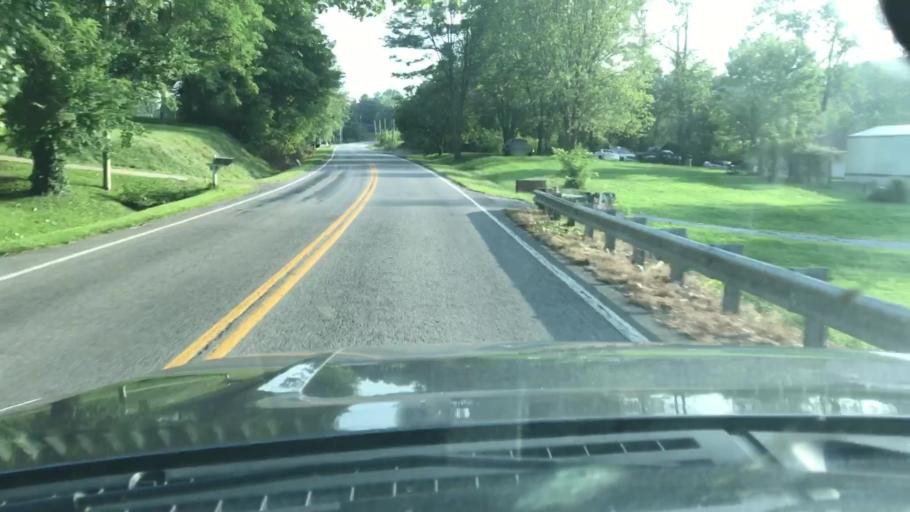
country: US
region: Tennessee
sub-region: Sumner County
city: Gallatin
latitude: 36.4834
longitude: -86.4374
